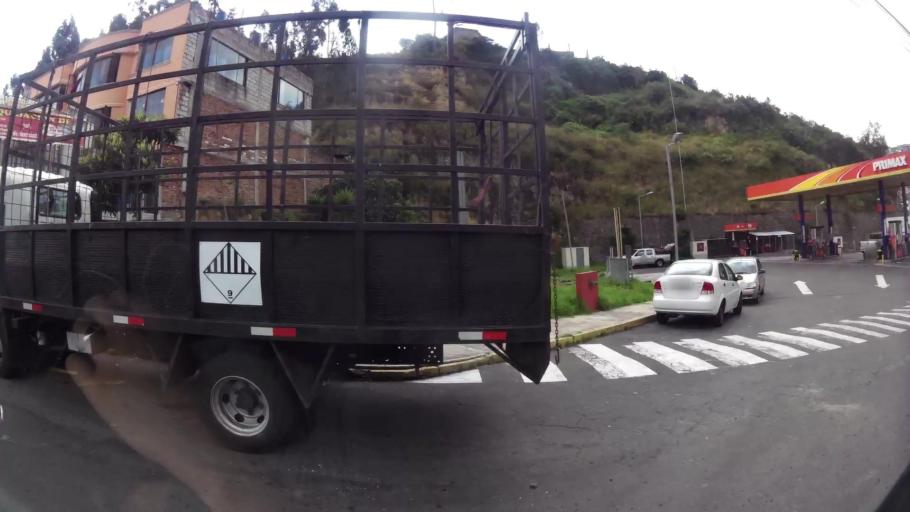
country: EC
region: Pichincha
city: Quito
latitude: -0.2468
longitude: -78.5057
